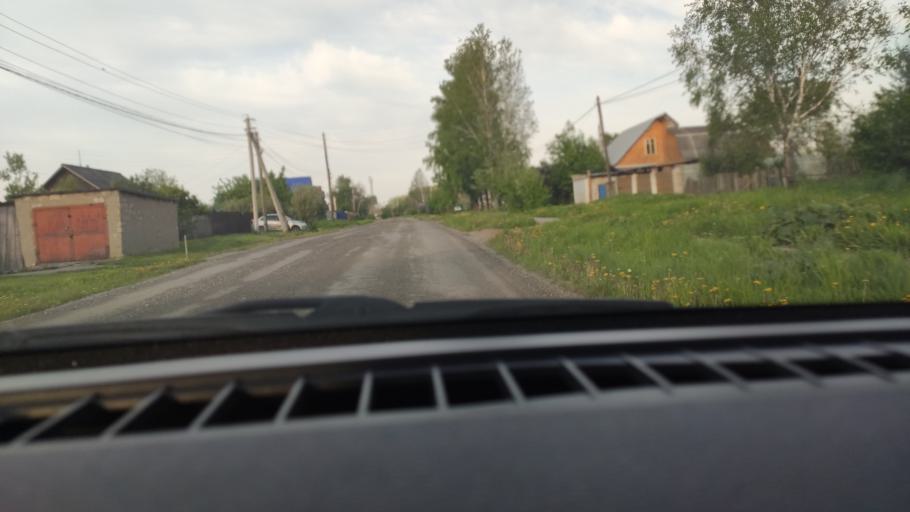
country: RU
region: Perm
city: Kondratovo
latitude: 57.9381
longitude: 56.0378
